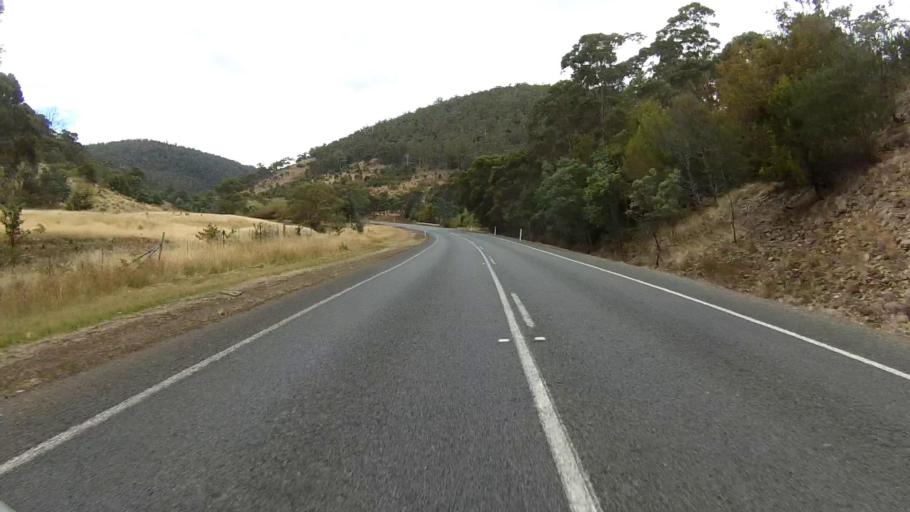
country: AU
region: Tasmania
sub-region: Sorell
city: Sorell
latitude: -42.6833
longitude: 147.5301
